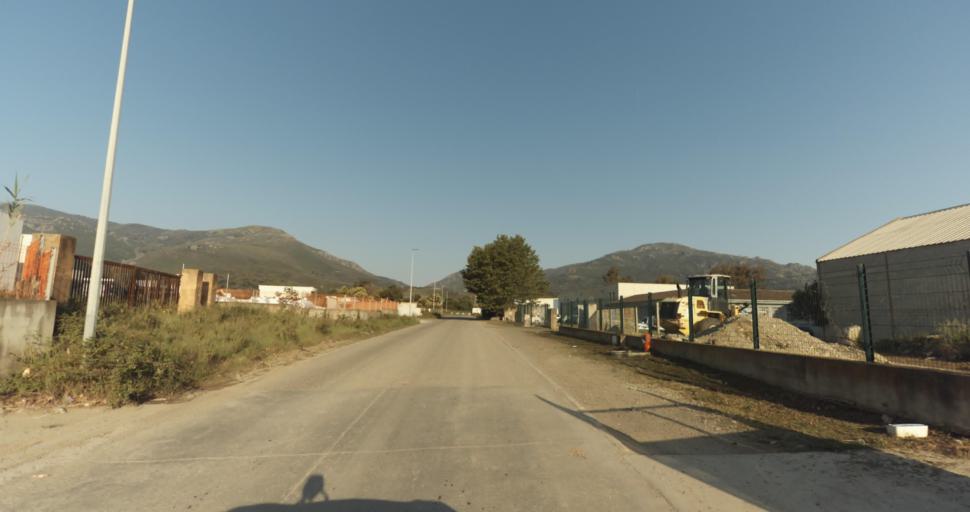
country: FR
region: Corsica
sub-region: Departement de la Haute-Corse
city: Biguglia
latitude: 42.5997
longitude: 9.4458
